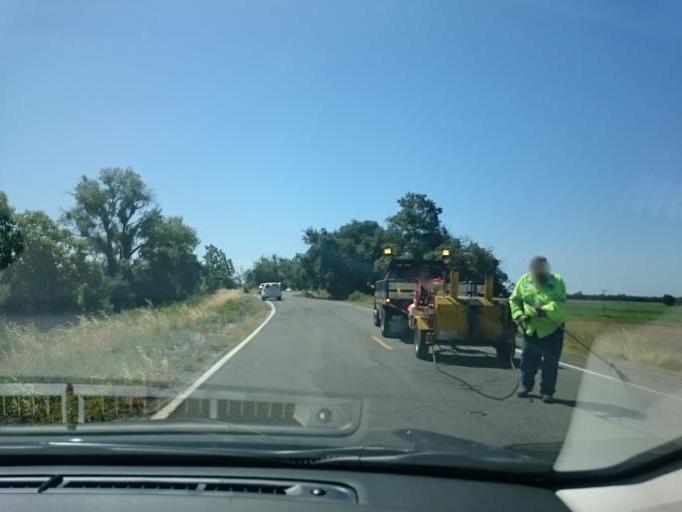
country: US
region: California
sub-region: Yolo County
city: West Sacramento
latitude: 38.4916
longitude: -121.5565
